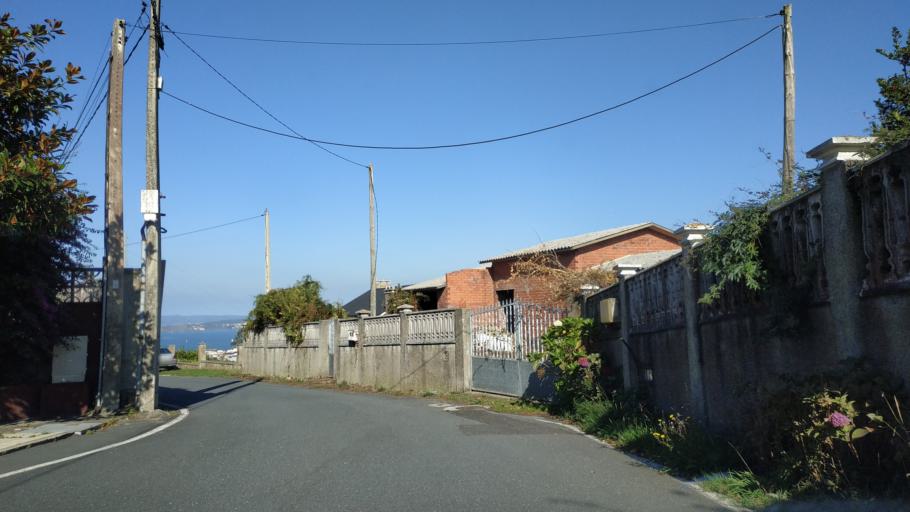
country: ES
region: Galicia
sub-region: Provincia da Coruna
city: Culleredo
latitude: 43.3224
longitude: -8.3863
